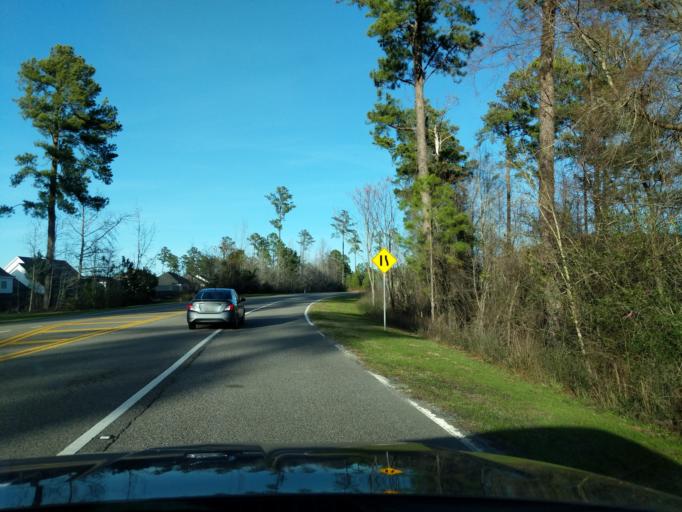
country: US
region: Georgia
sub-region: Columbia County
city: Evans
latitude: 33.5786
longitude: -82.2050
